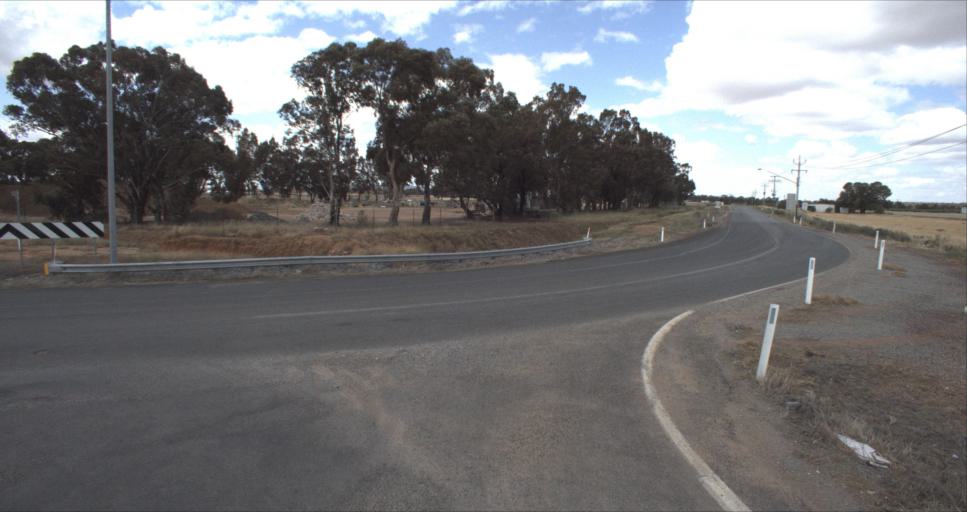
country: AU
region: New South Wales
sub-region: Leeton
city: Leeton
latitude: -34.5716
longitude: 146.3945
